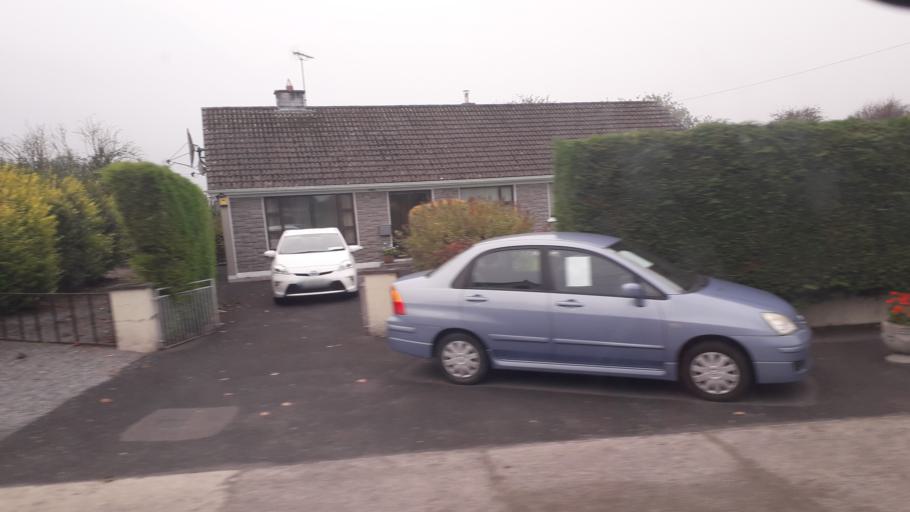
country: IE
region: Leinster
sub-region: Uibh Fhaili
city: Birr
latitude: 52.9870
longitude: -7.9227
